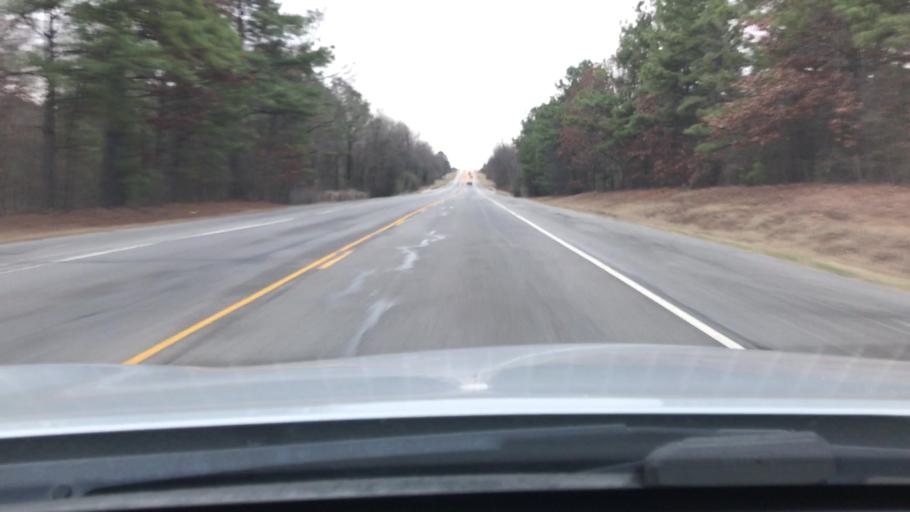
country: US
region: Arkansas
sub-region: Hempstead County
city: Hope
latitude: 33.6808
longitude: -93.5755
